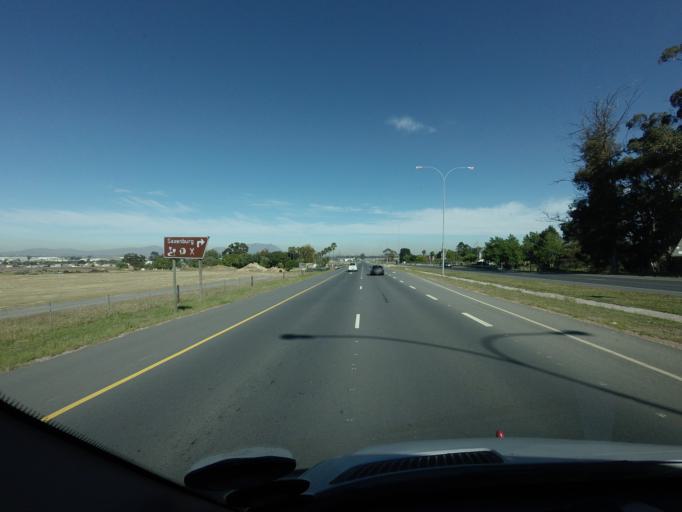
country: ZA
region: Western Cape
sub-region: City of Cape Town
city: Kraaifontein
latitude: -33.9520
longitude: 18.7140
